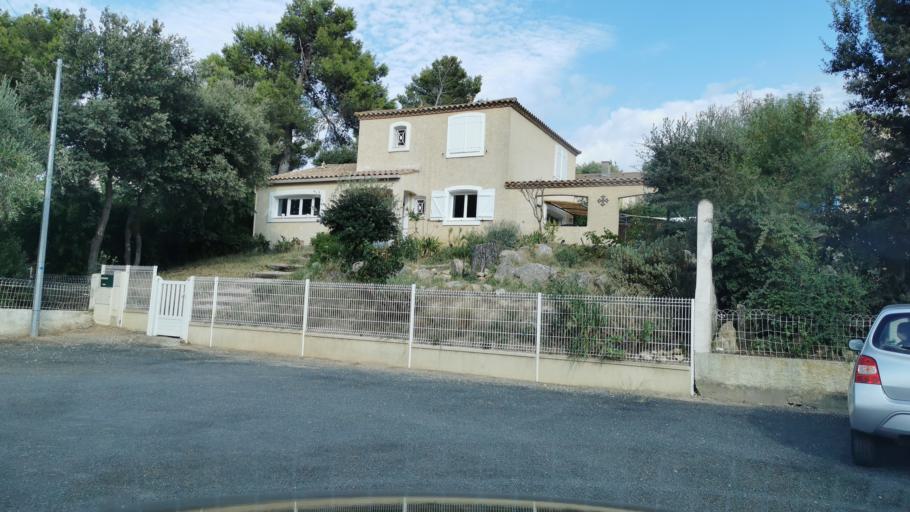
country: FR
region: Languedoc-Roussillon
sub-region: Departement de l'Aude
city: Moussan
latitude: 43.2349
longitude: 2.9370
